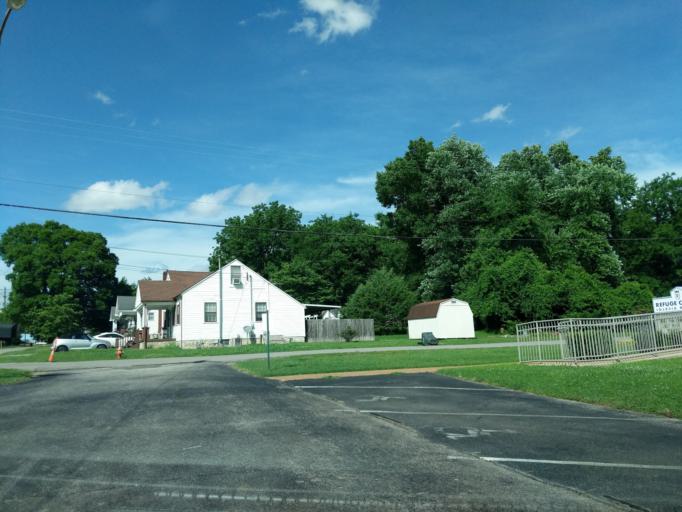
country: US
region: Tennessee
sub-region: Davidson County
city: Lakewood
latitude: 36.2709
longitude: -86.6676
